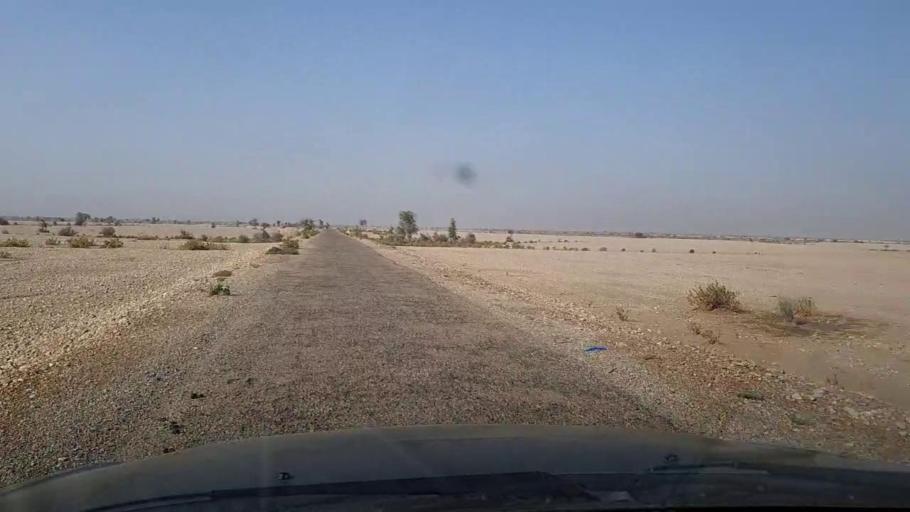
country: PK
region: Sindh
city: Sann
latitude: 25.9965
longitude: 68.0739
